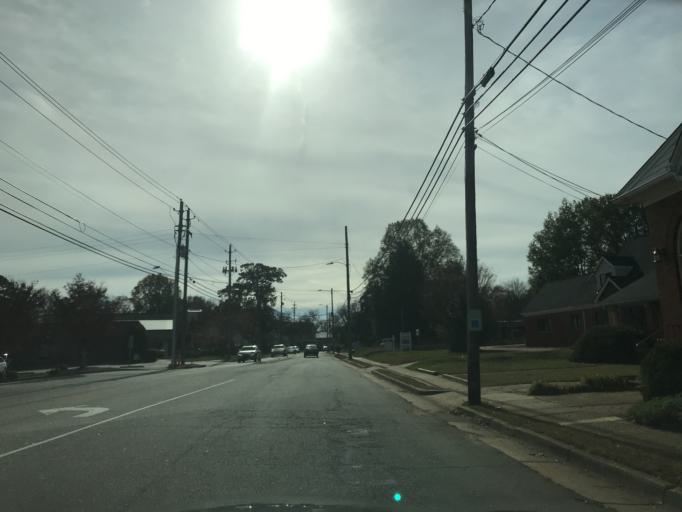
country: US
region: North Carolina
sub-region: Wake County
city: West Raleigh
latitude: 35.7978
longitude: -78.6601
